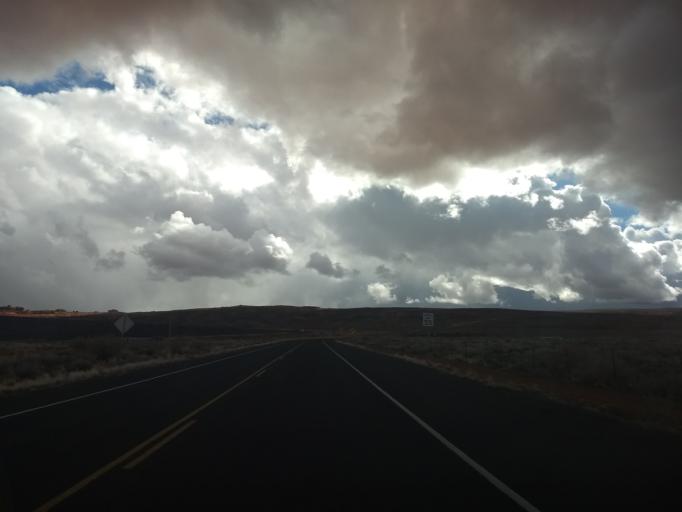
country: US
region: Utah
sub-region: Washington County
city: Hurricane
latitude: 37.1147
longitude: -113.3913
